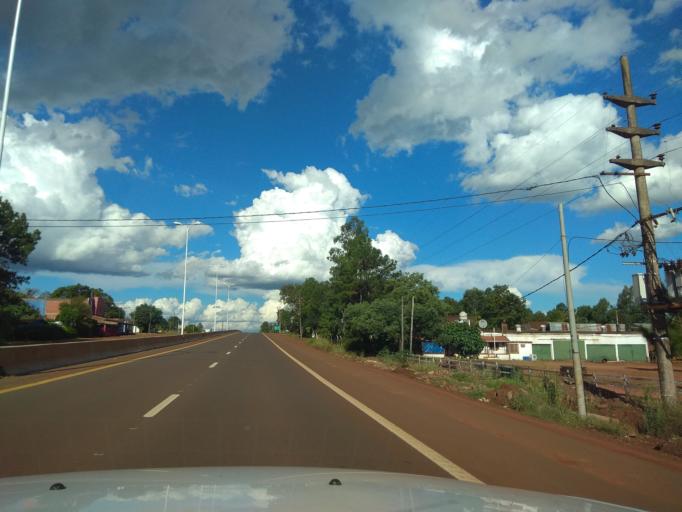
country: AR
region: Misiones
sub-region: Departamento de Candelaria
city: Candelaria
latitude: -27.4716
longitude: -55.7393
